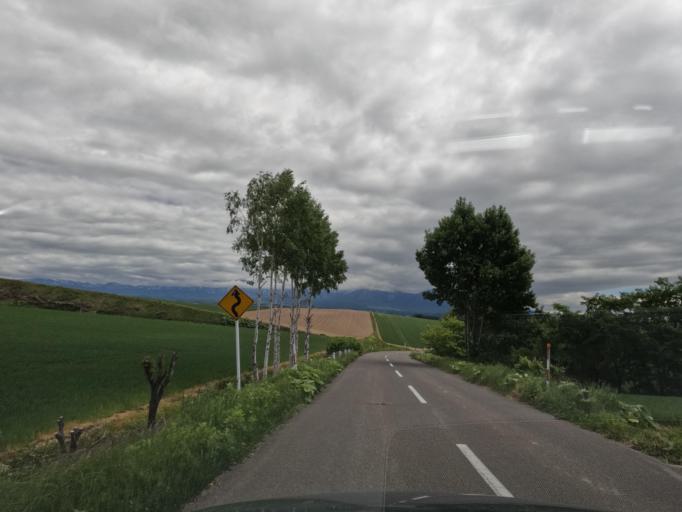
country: JP
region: Hokkaido
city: Shimo-furano
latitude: 43.4993
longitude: 142.4138
